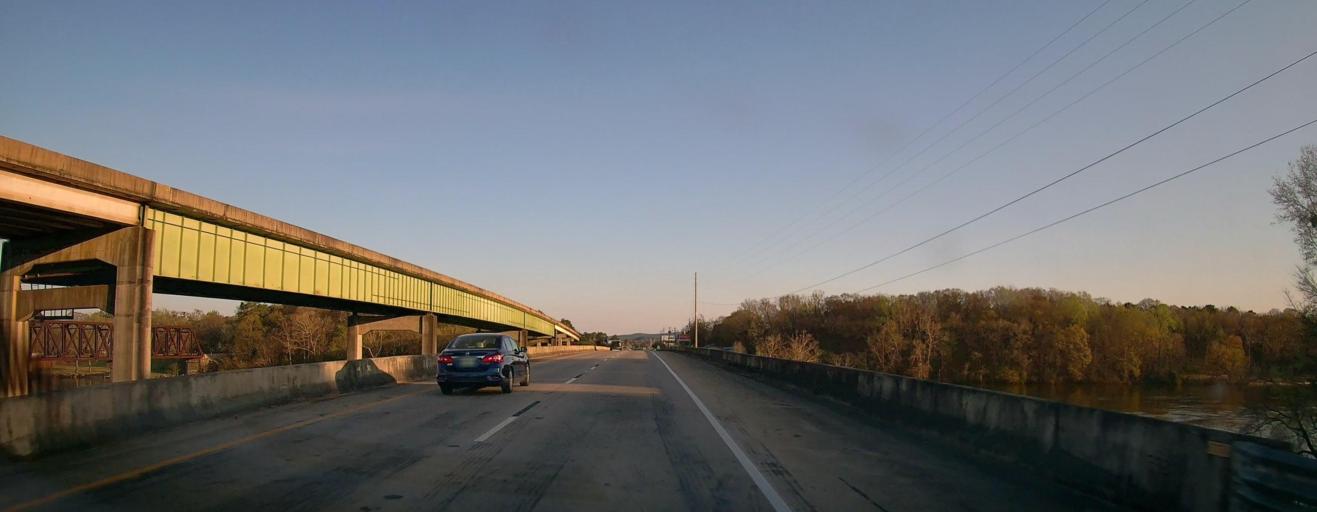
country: US
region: Alabama
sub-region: Talladega County
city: Childersburg
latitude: 33.2917
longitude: -86.3658
